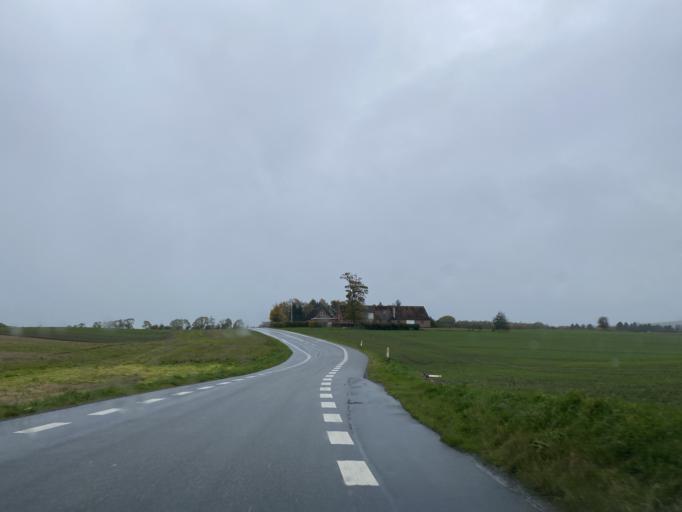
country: DK
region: Central Jutland
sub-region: Silkeborg Kommune
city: Svejbaek
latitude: 56.1735
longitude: 9.6936
